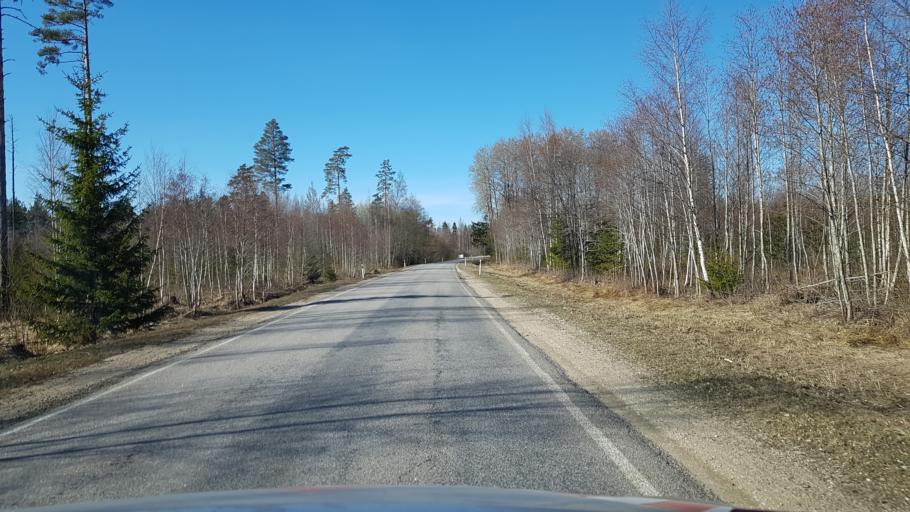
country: EE
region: Laeaene-Virumaa
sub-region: Vinni vald
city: Vinni
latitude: 59.2452
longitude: 26.6897
